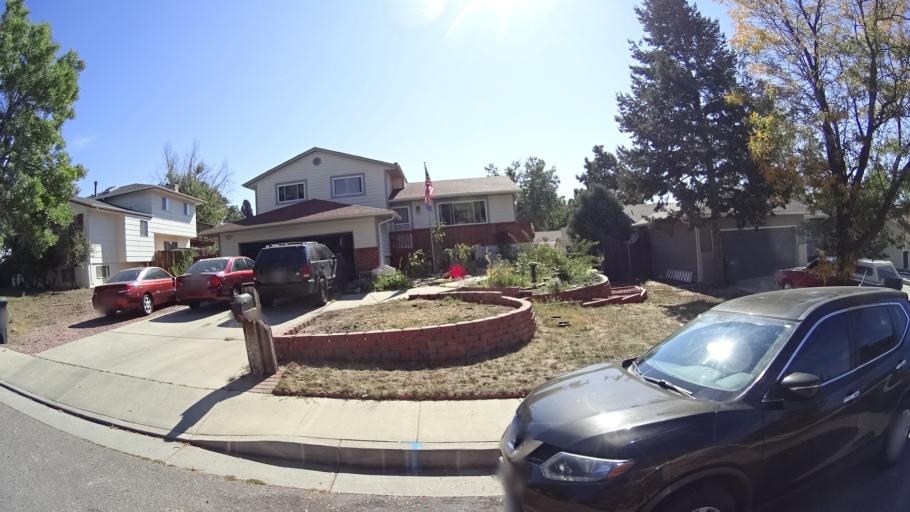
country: US
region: Colorado
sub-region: El Paso County
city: Cimarron Hills
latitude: 38.9173
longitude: -104.7703
